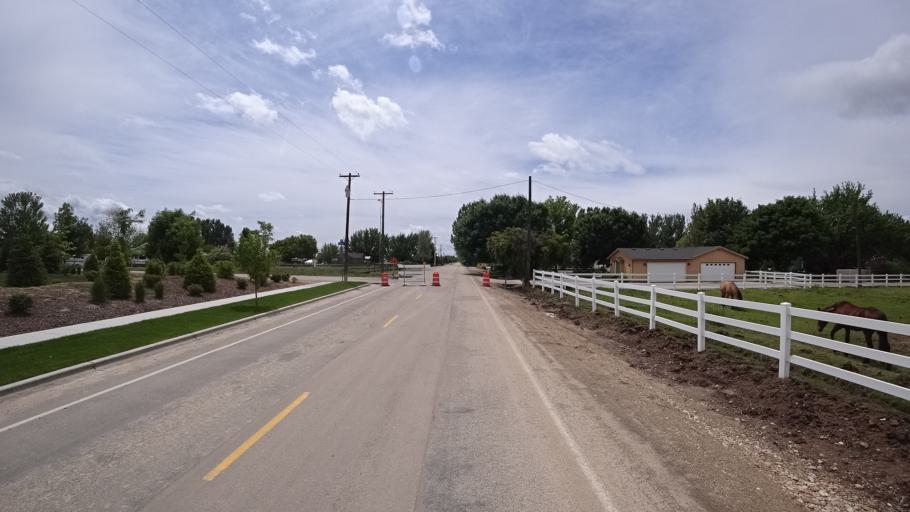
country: US
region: Idaho
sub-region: Ada County
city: Eagle
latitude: 43.7174
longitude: -116.4035
